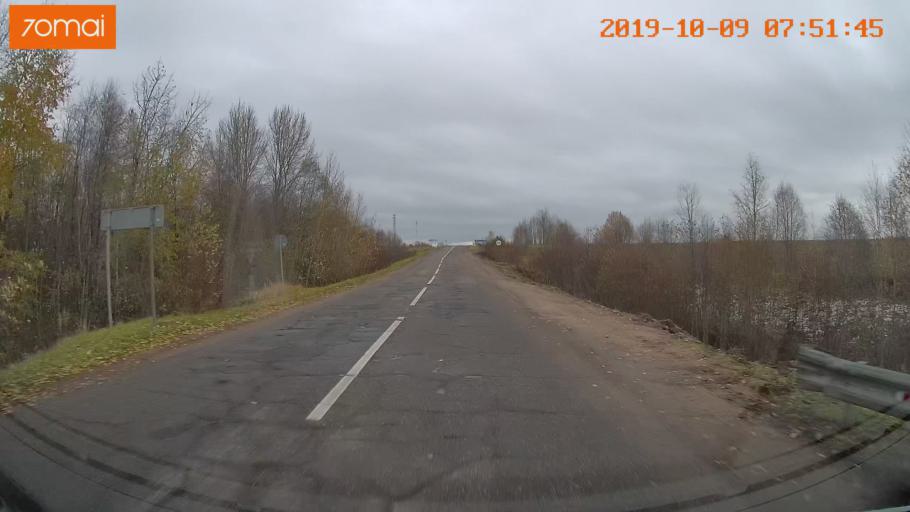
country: RU
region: Jaroslavl
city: Kukoboy
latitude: 58.6855
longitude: 39.8811
